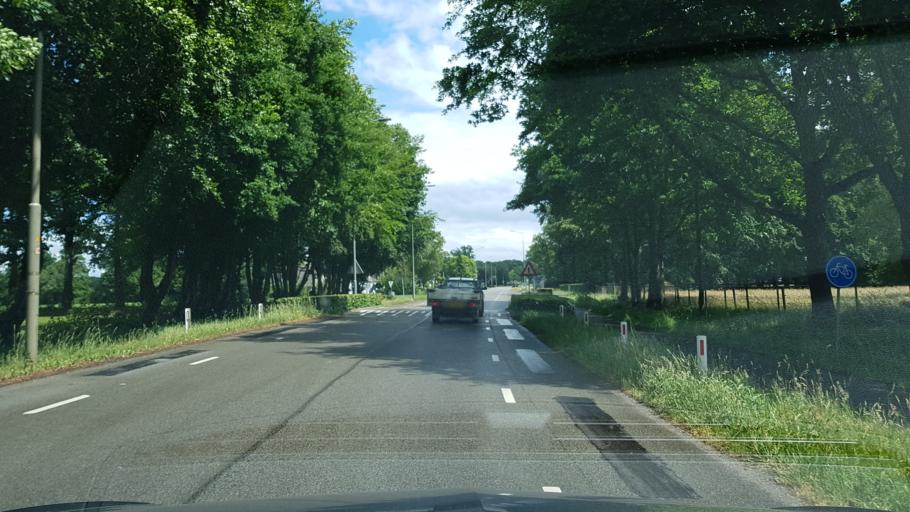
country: NL
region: Gelderland
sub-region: Gemeente Nunspeet
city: Nunspeet
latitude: 52.3602
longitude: 5.7194
